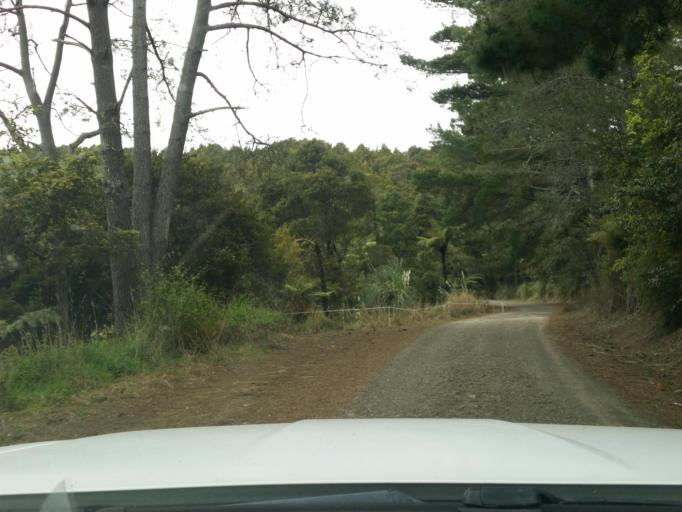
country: NZ
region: Northland
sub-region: Kaipara District
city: Dargaville
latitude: -35.7088
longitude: 173.6233
